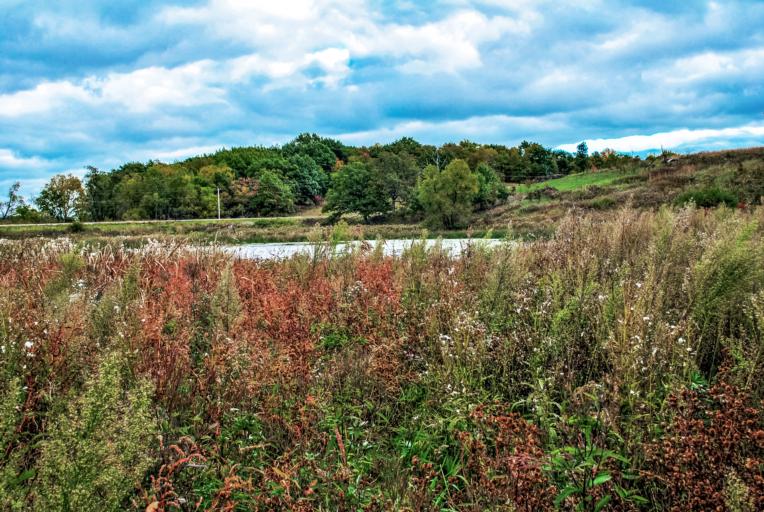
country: US
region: Wisconsin
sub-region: Jefferson County
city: Lake Mills
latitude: 43.1239
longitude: -88.9154
